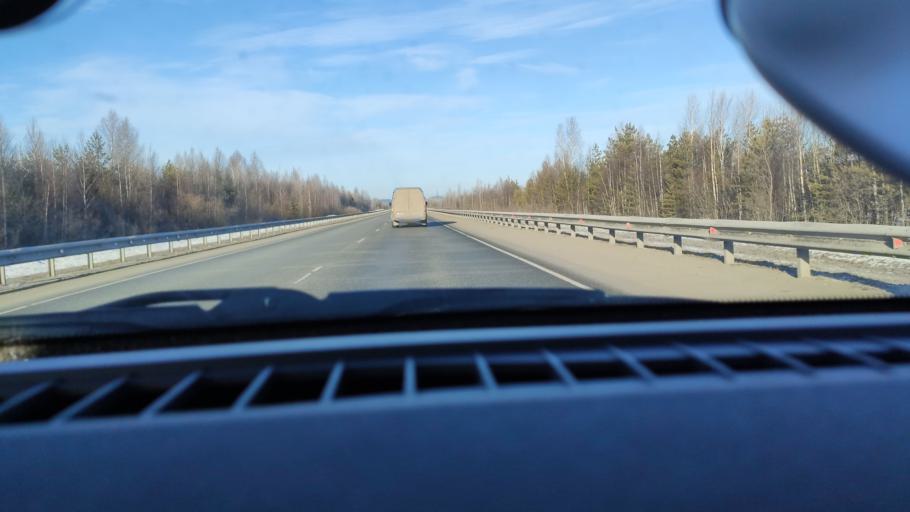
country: RU
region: Perm
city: Krasnokamsk
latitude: 58.0878
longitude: 55.6910
